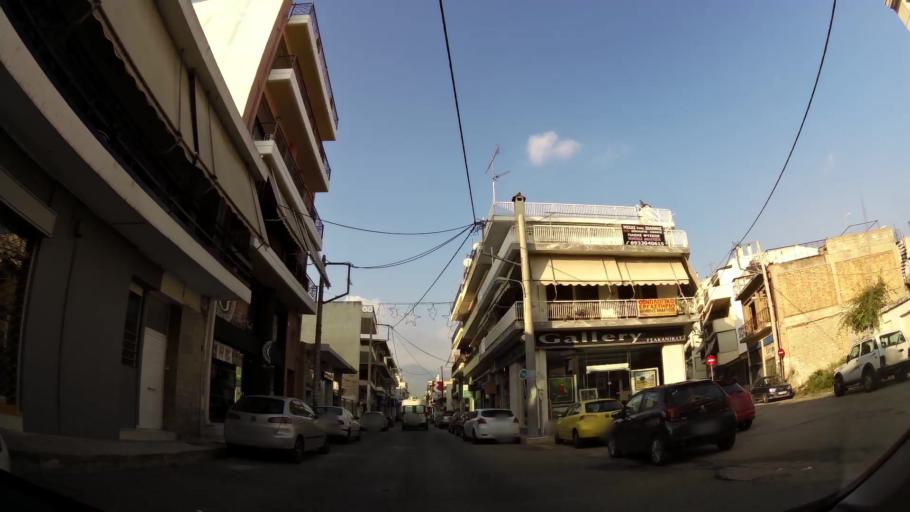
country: GR
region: Attica
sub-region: Nomarchia Anatolikis Attikis
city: Acharnes
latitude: 38.0841
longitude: 23.7374
